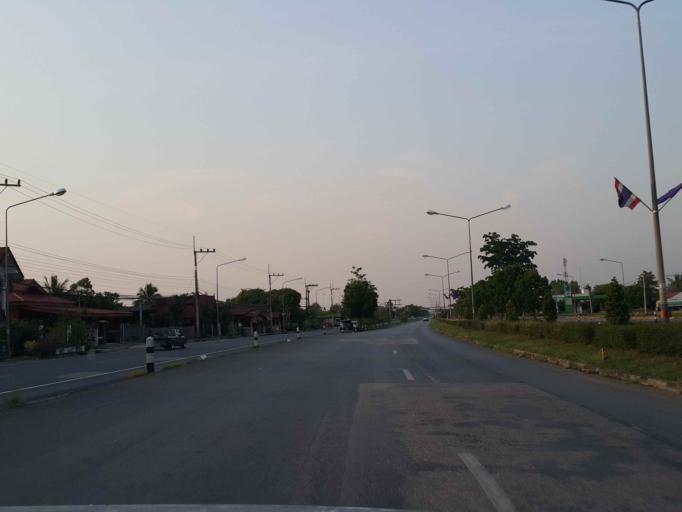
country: TH
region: Lampang
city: Sop Prap
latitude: 17.8757
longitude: 99.3370
